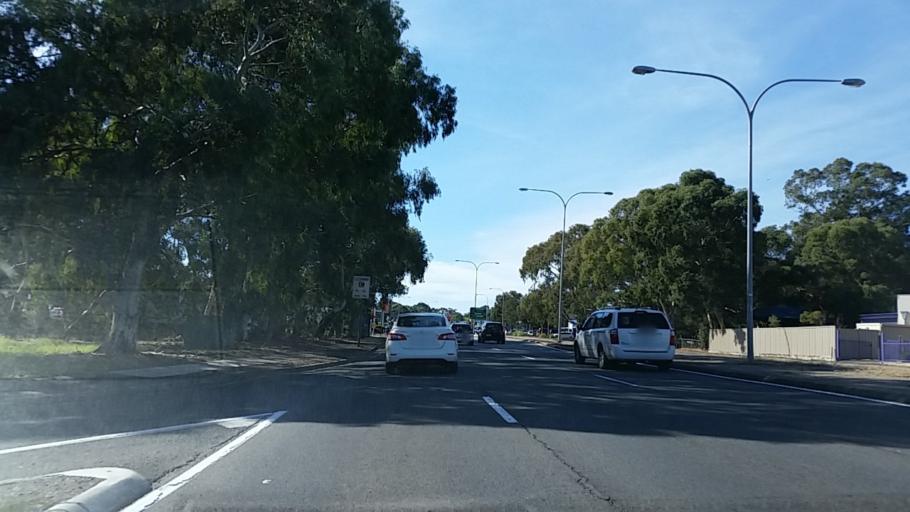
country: AU
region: South Australia
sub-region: Tea Tree Gully
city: Modbury
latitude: -34.8354
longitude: 138.6808
